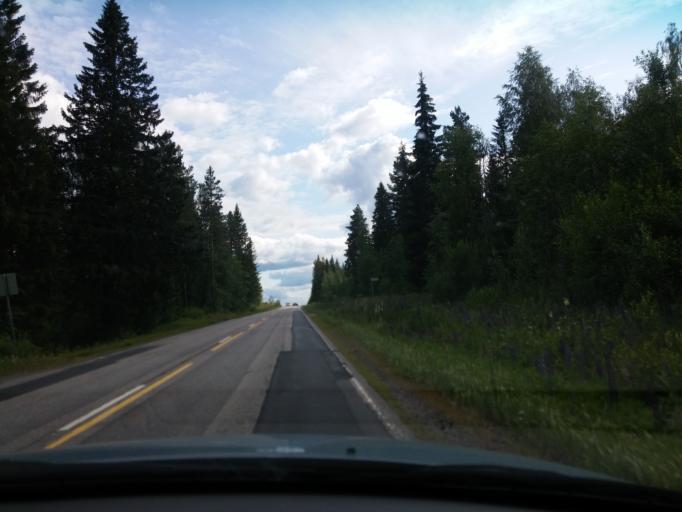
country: FI
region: Central Finland
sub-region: Keuruu
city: Keuruu
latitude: 62.3282
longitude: 24.7331
